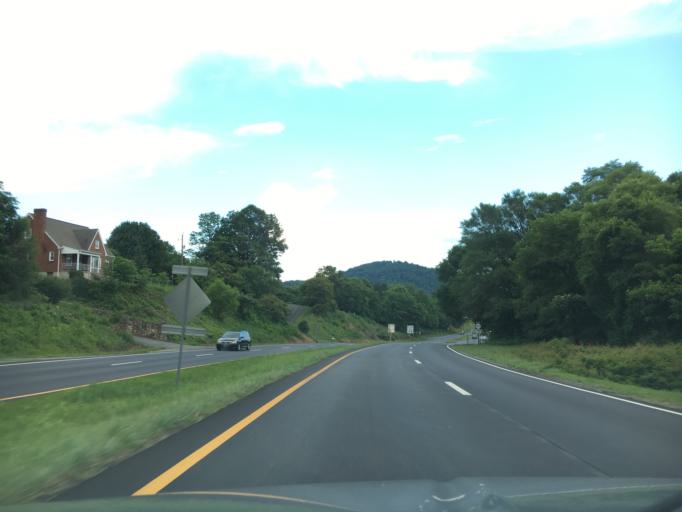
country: US
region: Virginia
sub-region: Roanoke County
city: Vinton
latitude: 37.2843
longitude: -79.8442
